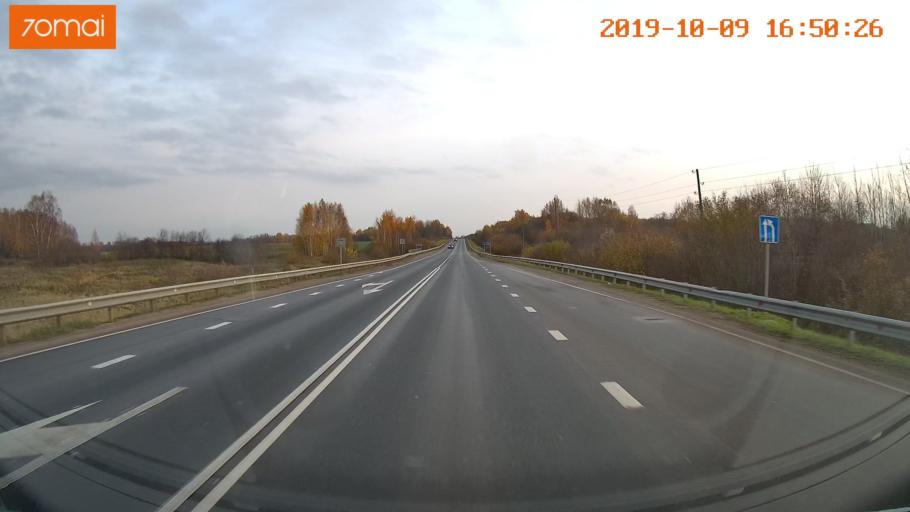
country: RU
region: Kostroma
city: Volgorechensk
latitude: 57.4009
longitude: 41.2089
